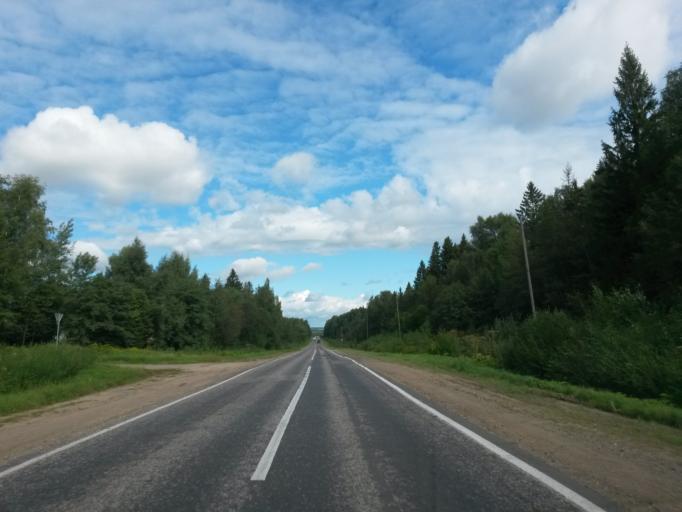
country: RU
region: Jaroslavl
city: Yaroslavl
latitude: 57.4941
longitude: 39.9007
